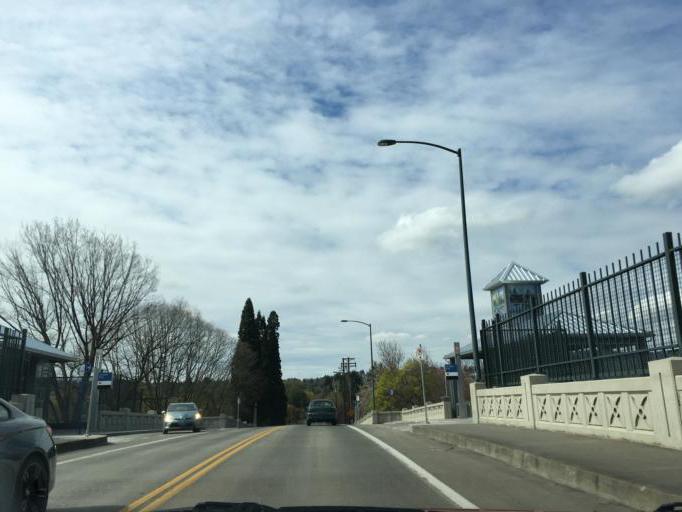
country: US
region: Oregon
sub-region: Clackamas County
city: Milwaukie
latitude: 45.4743
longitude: -122.6395
